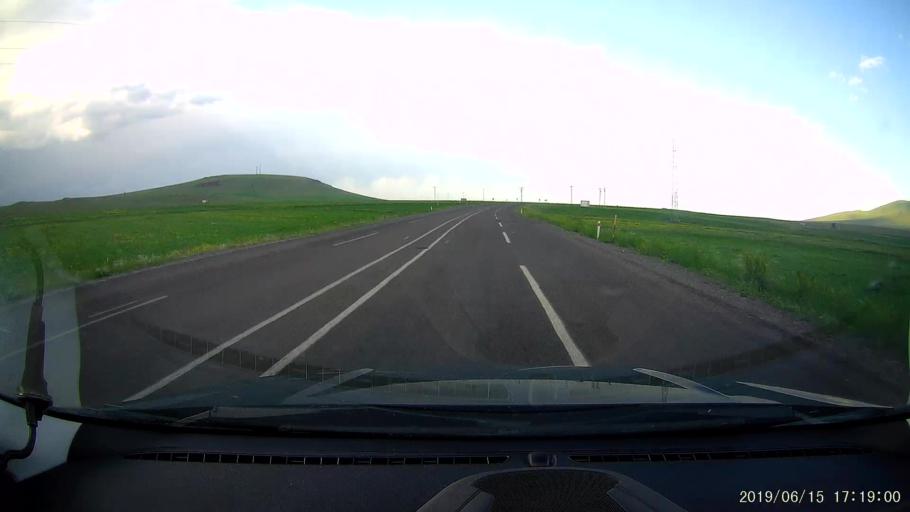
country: TR
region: Kars
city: Kars
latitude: 40.6152
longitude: 43.2699
